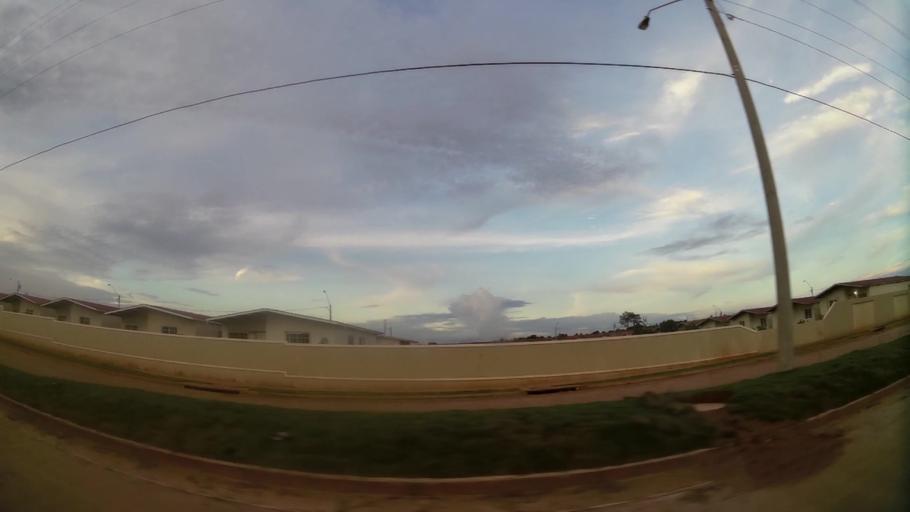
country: PA
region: Panama
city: La Mitra
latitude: 8.8562
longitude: -79.7575
